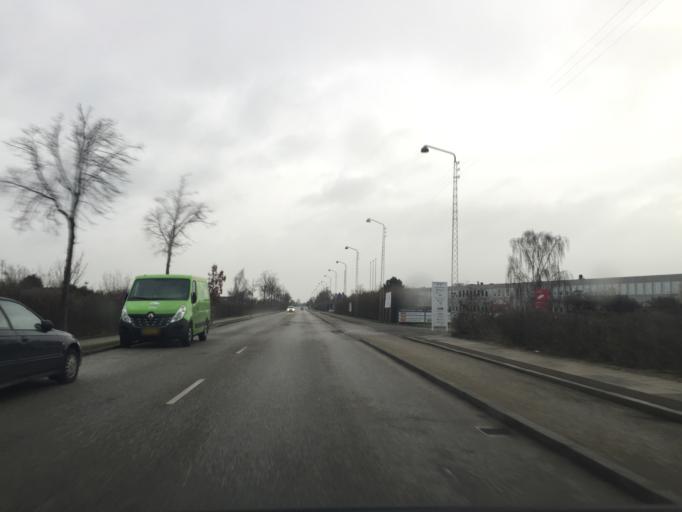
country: DK
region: Capital Region
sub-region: Tarnby Kommune
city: Tarnby
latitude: 55.6247
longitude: 12.5923
